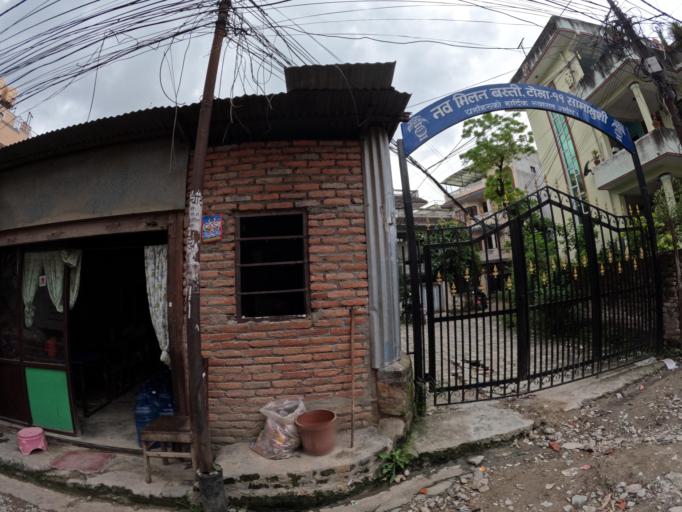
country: NP
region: Central Region
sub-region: Bagmati Zone
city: Kathmandu
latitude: 27.7395
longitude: 85.3174
